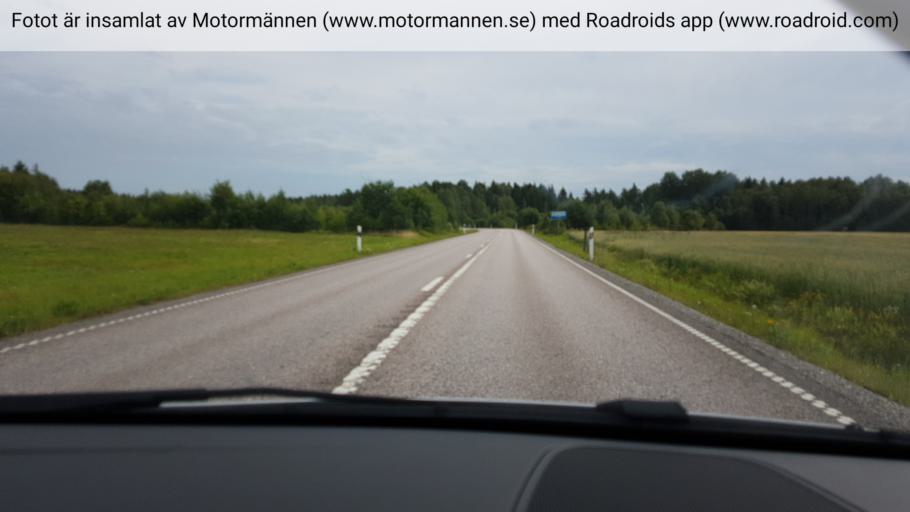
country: SE
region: Stockholm
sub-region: Norrtalje Kommun
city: Hallstavik
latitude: 60.0476
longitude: 18.5285
